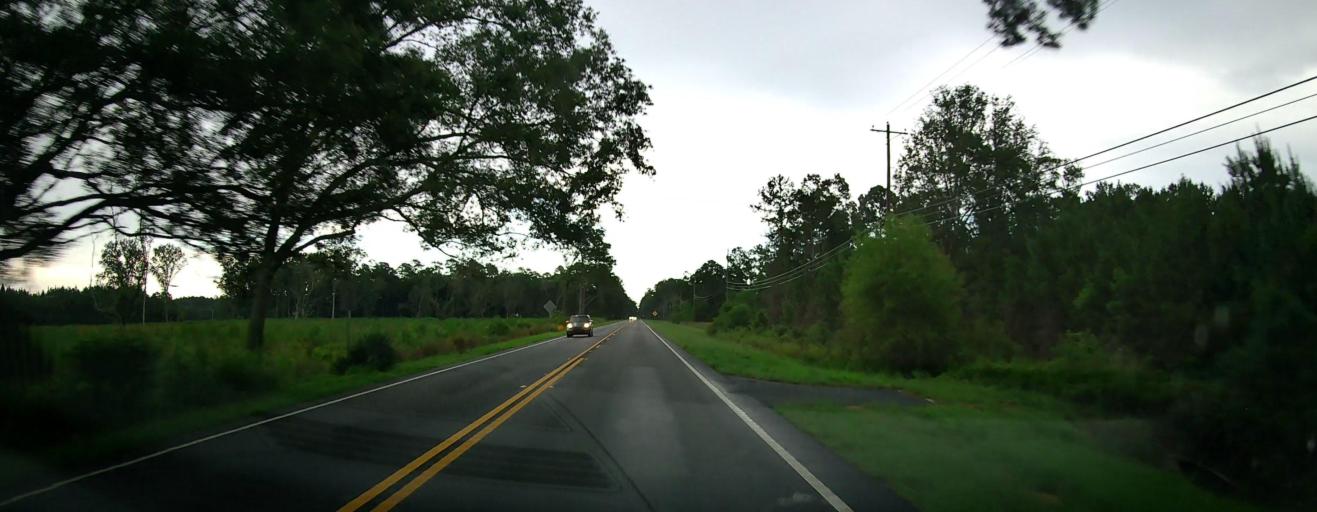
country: US
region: Georgia
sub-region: Glynn County
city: Dock Junction
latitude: 31.2908
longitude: -81.6889
